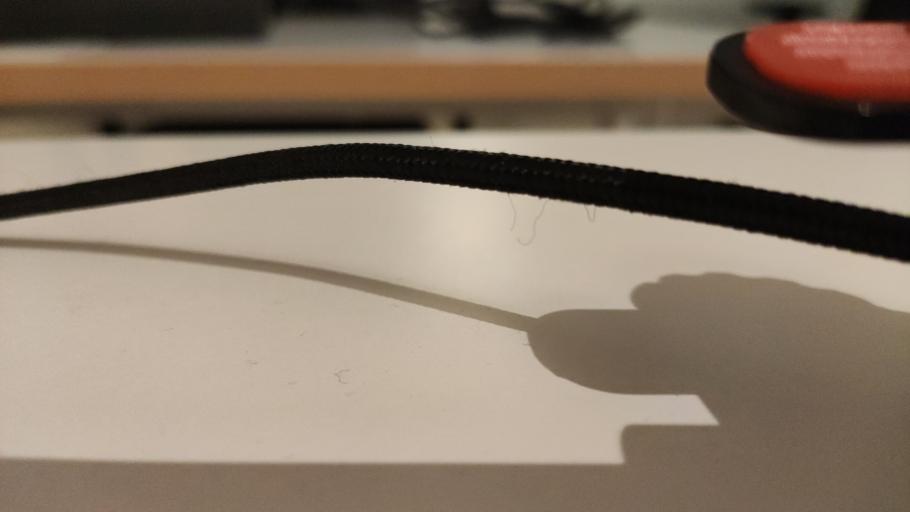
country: RU
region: Moskovskaya
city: Likino-Dulevo
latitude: 55.6977
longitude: 38.9548
